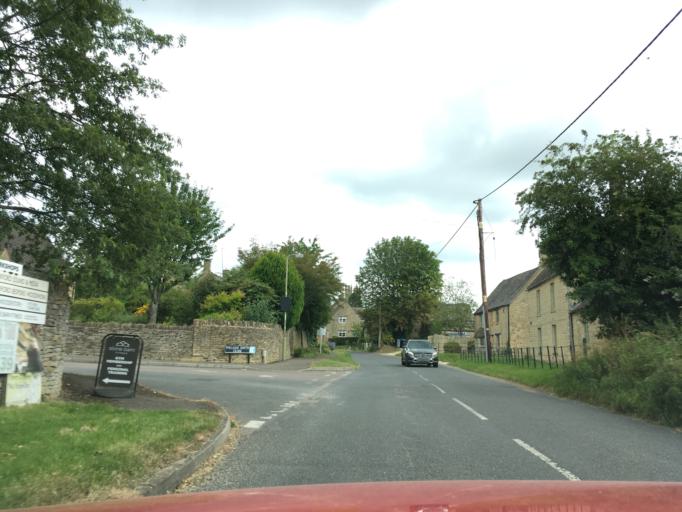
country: GB
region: England
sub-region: Oxfordshire
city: Shipton under Wychwood
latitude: 51.9123
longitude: -1.5920
